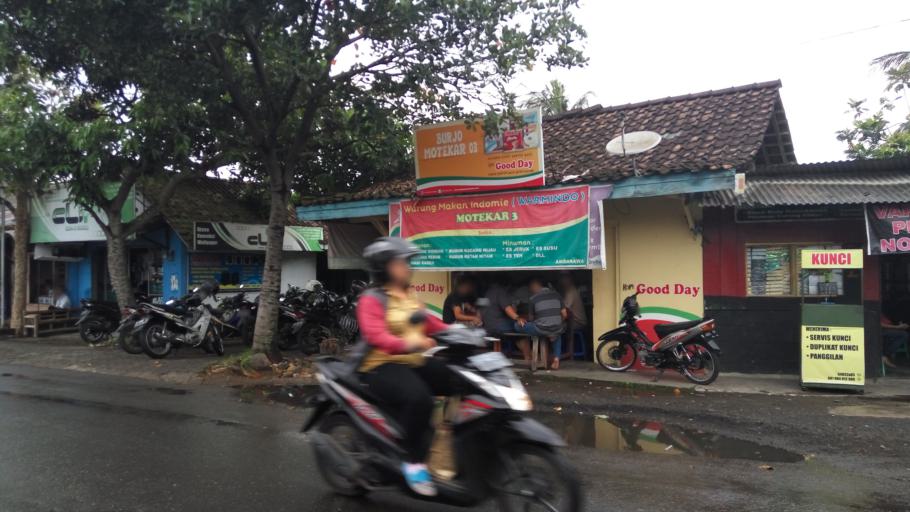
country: ID
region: Central Java
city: Ambarawa
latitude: -7.2669
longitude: 110.4076
